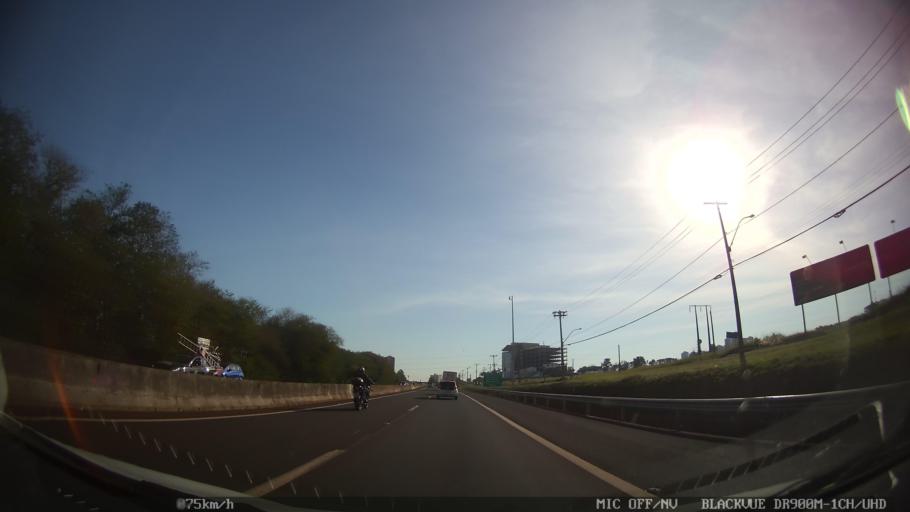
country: BR
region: Sao Paulo
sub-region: Ribeirao Preto
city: Ribeirao Preto
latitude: -21.2299
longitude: -47.8178
